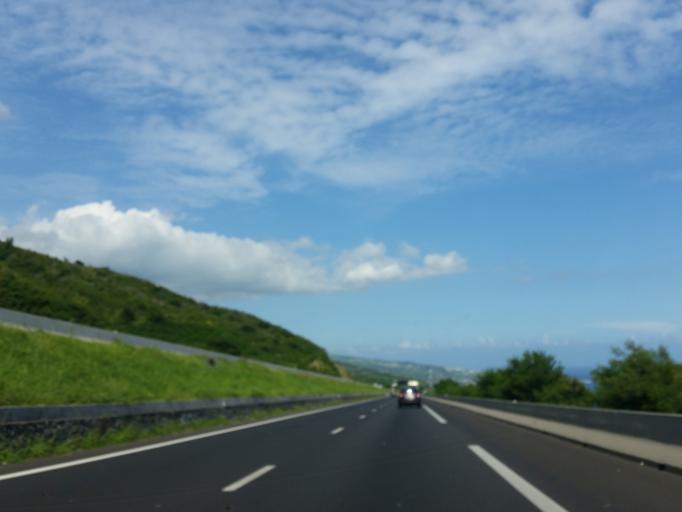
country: RE
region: Reunion
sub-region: Reunion
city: Trois-Bassins
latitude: -21.1109
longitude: 55.2747
